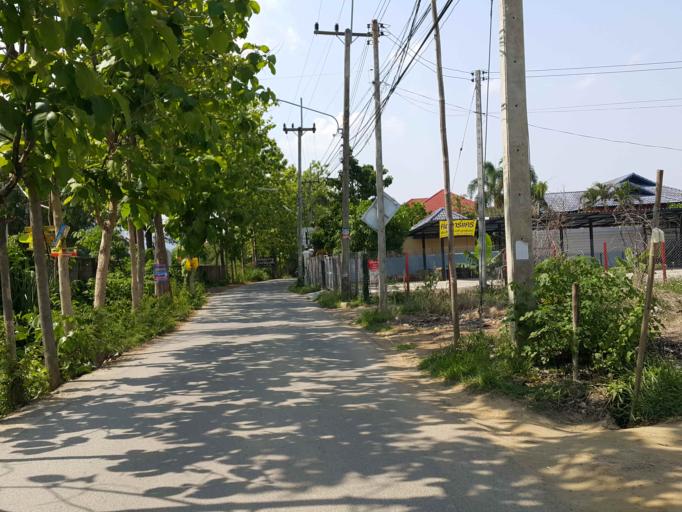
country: TH
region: Chiang Mai
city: Hang Dong
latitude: 18.7292
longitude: 98.9592
